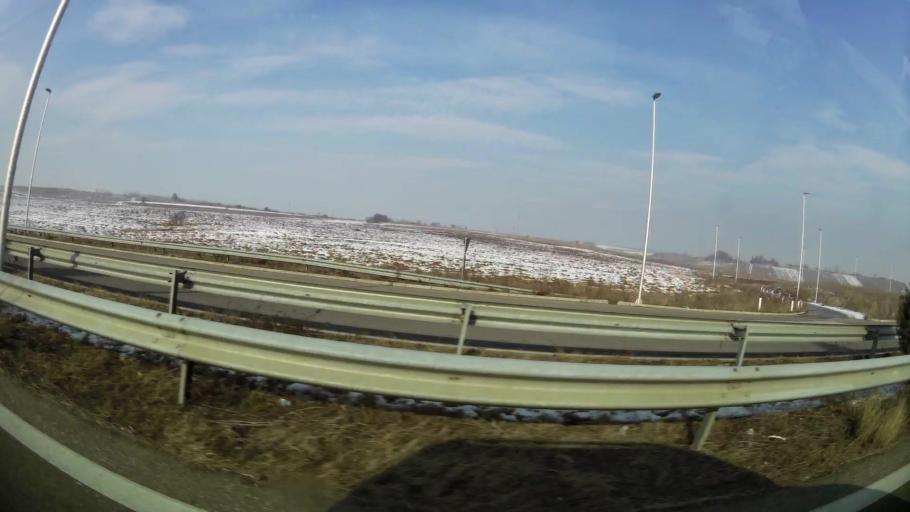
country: MK
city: Creshevo
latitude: 42.0326
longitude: 21.4836
